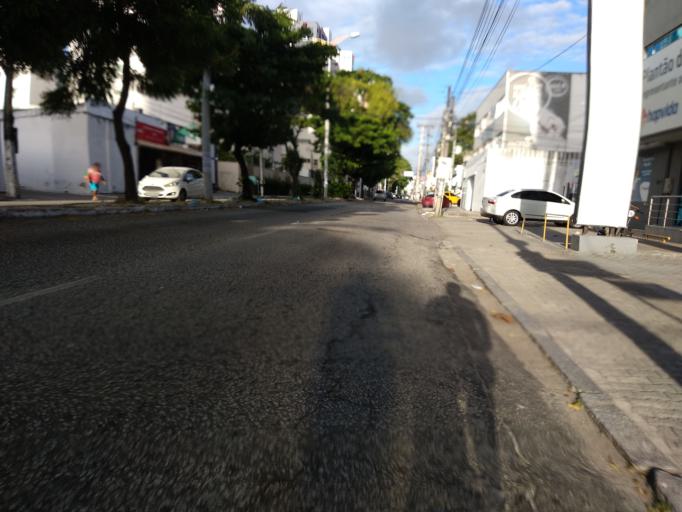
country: BR
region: Ceara
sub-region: Fortaleza
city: Fortaleza
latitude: -3.7342
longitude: -38.5221
